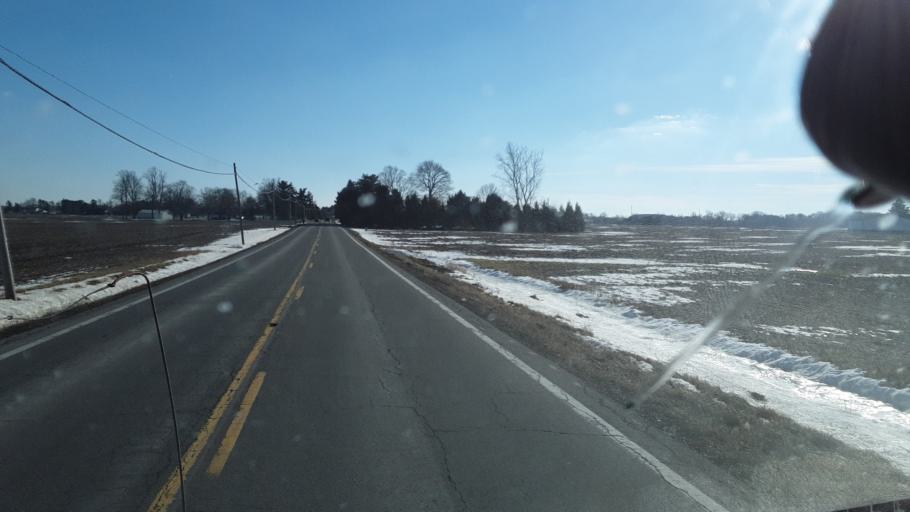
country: US
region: Ohio
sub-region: Richland County
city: Shelby
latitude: 40.9375
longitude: -82.6652
